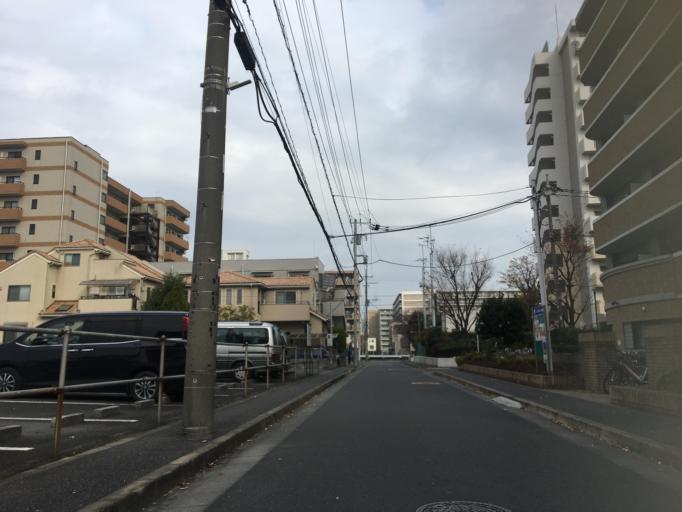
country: JP
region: Tokyo
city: Urayasu
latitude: 35.6579
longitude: 139.8819
